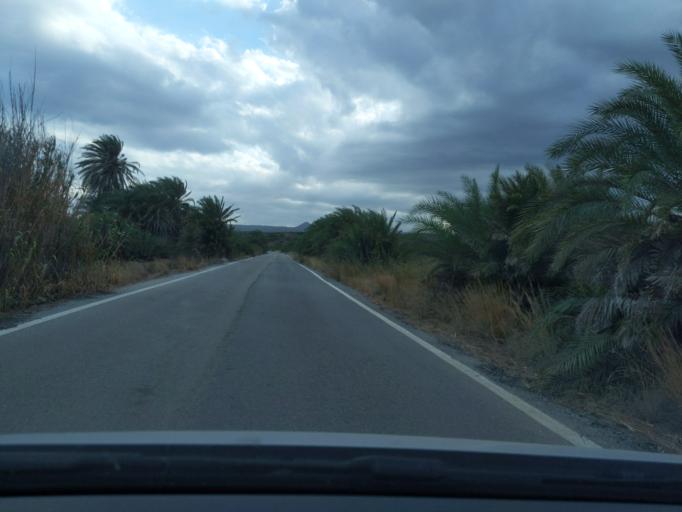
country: GR
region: Crete
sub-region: Nomos Lasithiou
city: Palekastro
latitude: 35.2573
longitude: 26.2548
